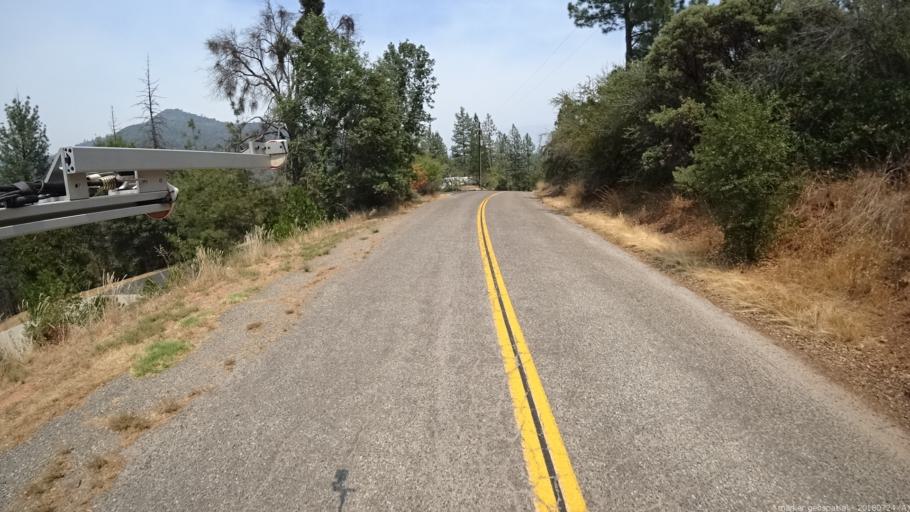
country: US
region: California
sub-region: Madera County
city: Oakhurst
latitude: 37.2474
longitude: -119.5562
